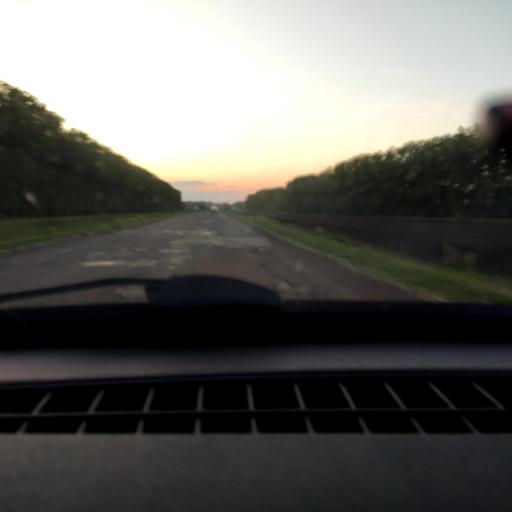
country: RU
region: Bashkortostan
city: Karmaskaly
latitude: 54.3933
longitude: 56.1717
